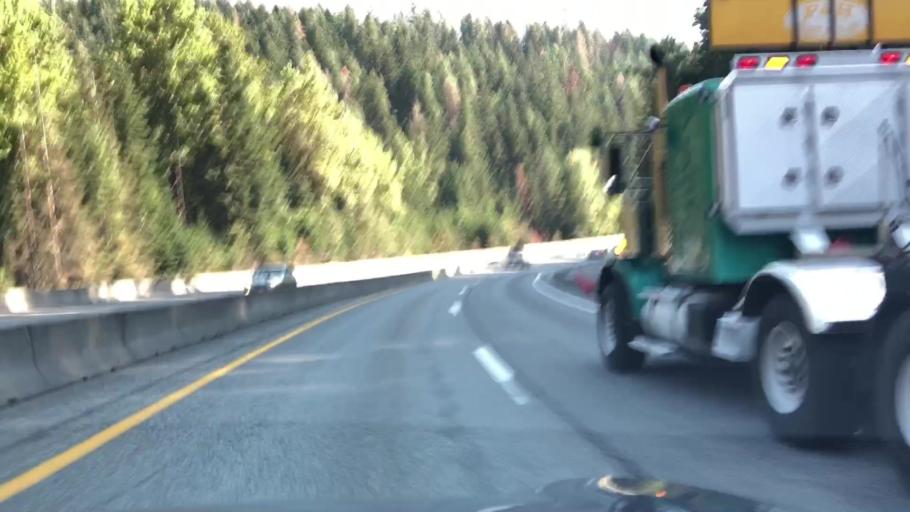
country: US
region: Idaho
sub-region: Shoshone County
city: Pinehurst
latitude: 47.5965
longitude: -116.4954
